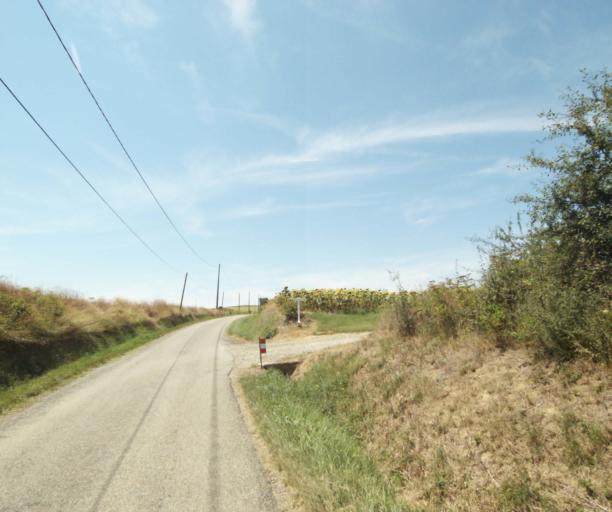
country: FR
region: Midi-Pyrenees
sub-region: Departement de l'Ariege
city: Lezat-sur-Leze
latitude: 43.2776
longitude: 1.3265
